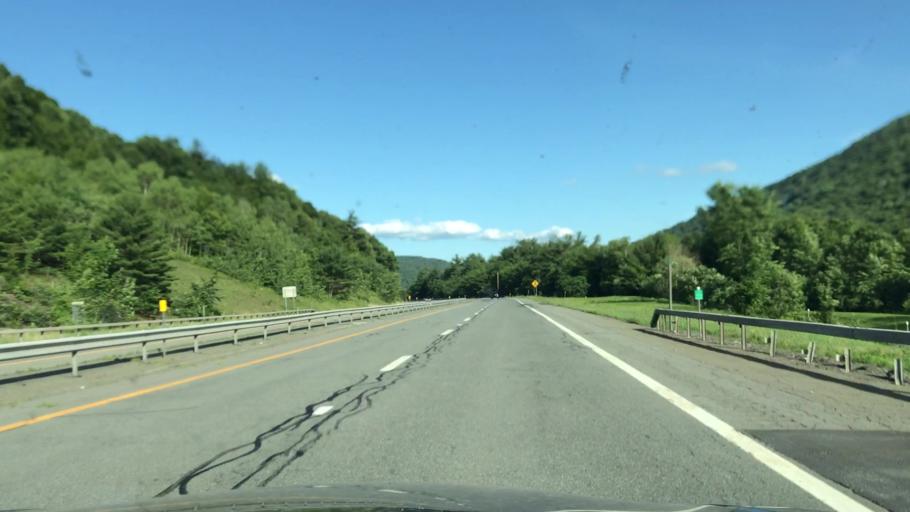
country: US
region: New York
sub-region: Delaware County
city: Hancock
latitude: 41.9905
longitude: -75.1282
